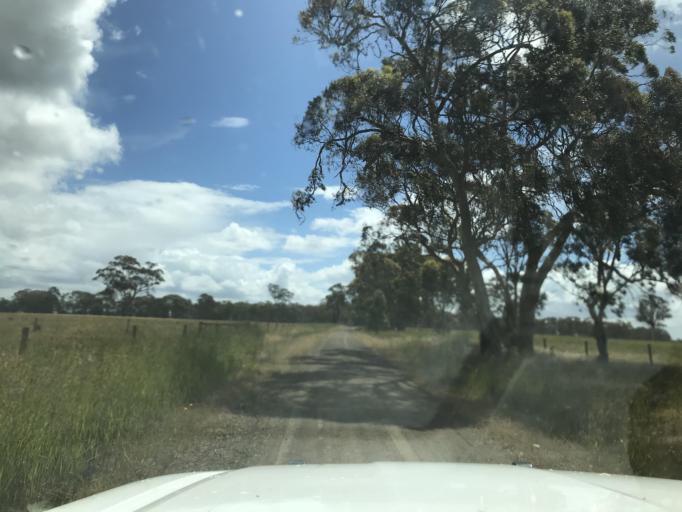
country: AU
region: South Australia
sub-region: Wattle Range
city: Penola
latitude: -37.1255
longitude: 141.3011
